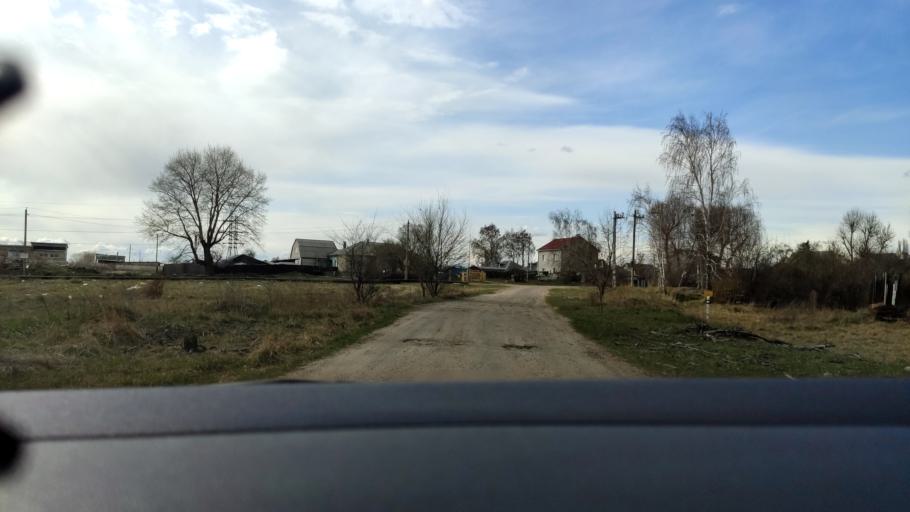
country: RU
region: Voronezj
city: Maslovka
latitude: 51.6279
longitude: 39.2787
